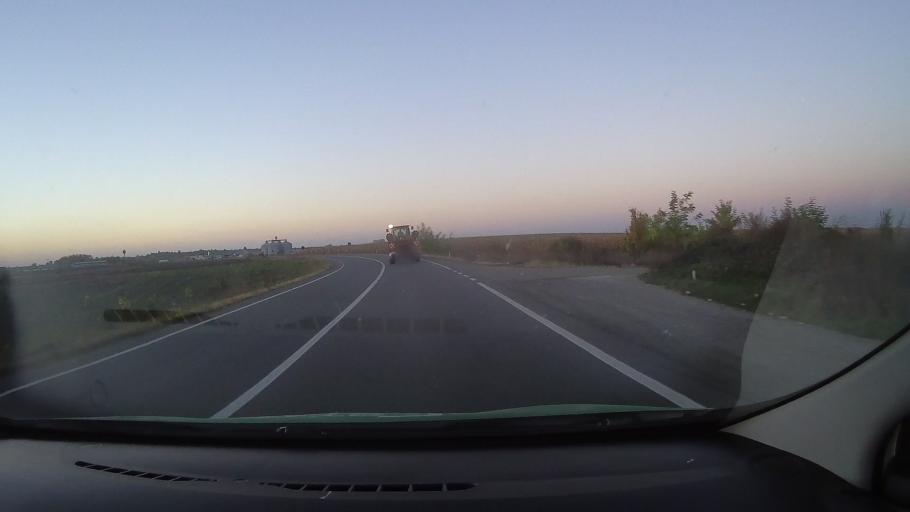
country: RO
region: Bihor
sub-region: Comuna Tarcea
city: Tarcea
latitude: 47.4488
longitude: 22.1854
